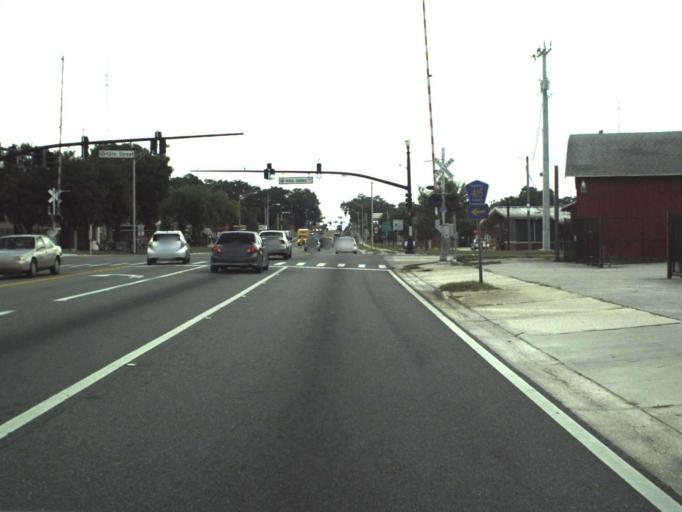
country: US
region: Florida
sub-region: Seminole County
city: Sanford
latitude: 28.8013
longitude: -81.2732
